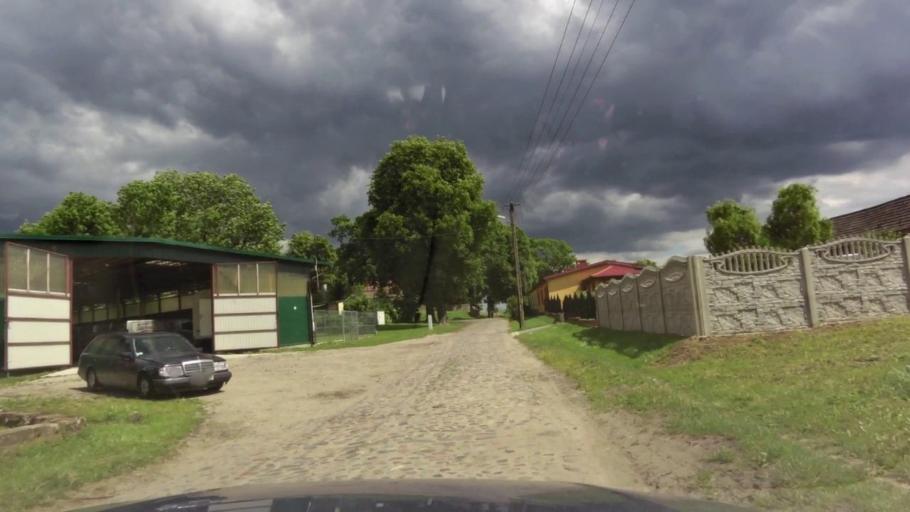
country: PL
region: West Pomeranian Voivodeship
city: Trzcinsko Zdroj
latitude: 52.9100
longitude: 14.5960
